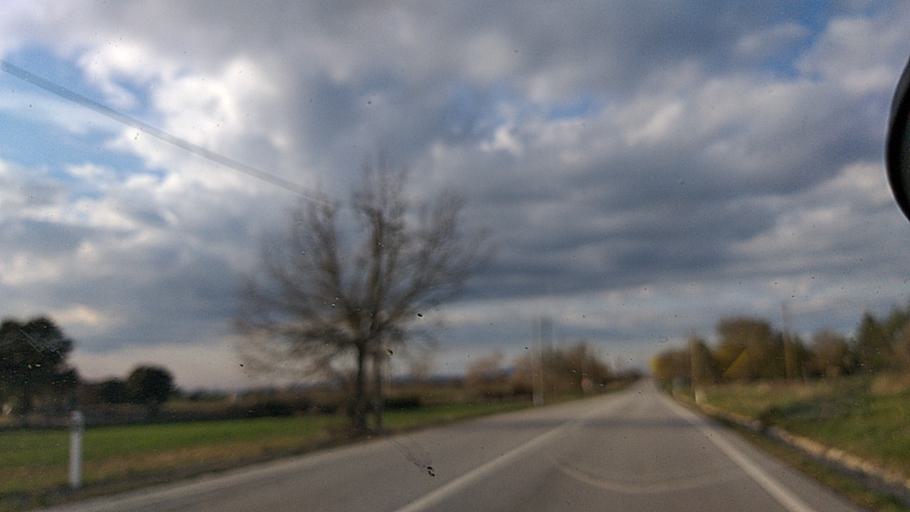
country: ES
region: Castille and Leon
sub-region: Provincia de Salamanca
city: Aldea del Obispo
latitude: 40.7060
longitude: -6.8964
